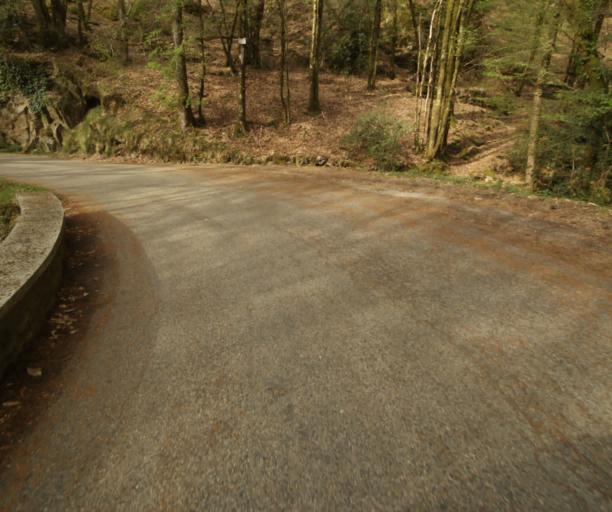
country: FR
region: Limousin
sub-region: Departement de la Correze
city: Argentat
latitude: 45.1961
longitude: 1.9802
